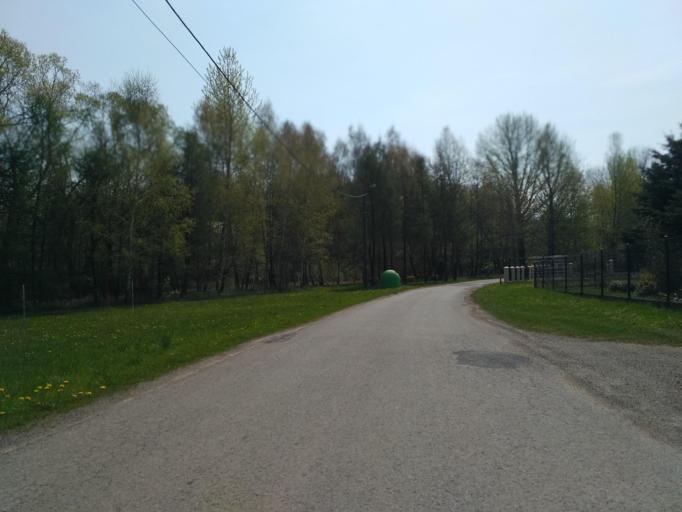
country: PL
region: Subcarpathian Voivodeship
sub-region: Powiat krosnienski
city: Miejsce Piastowe
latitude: 49.6322
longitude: 21.7308
